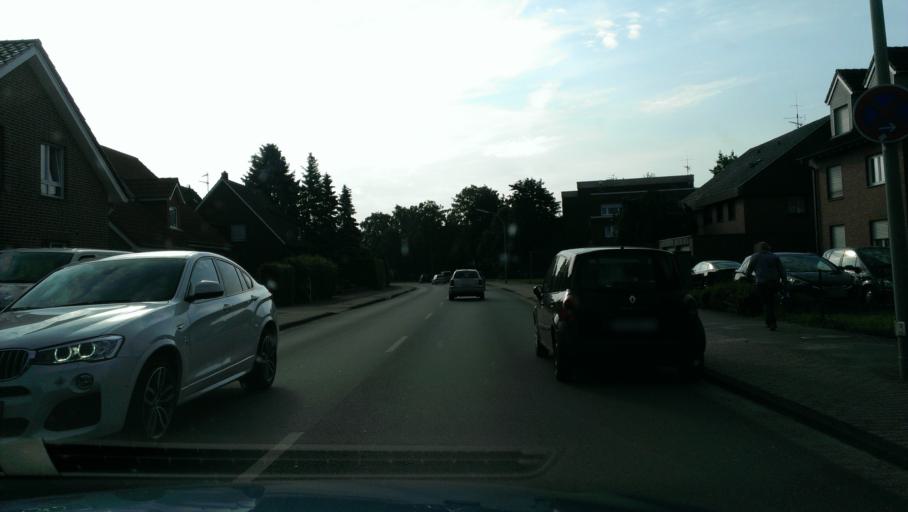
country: DE
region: North Rhine-Westphalia
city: Sendenhorst
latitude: 51.8424
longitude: 7.8351
